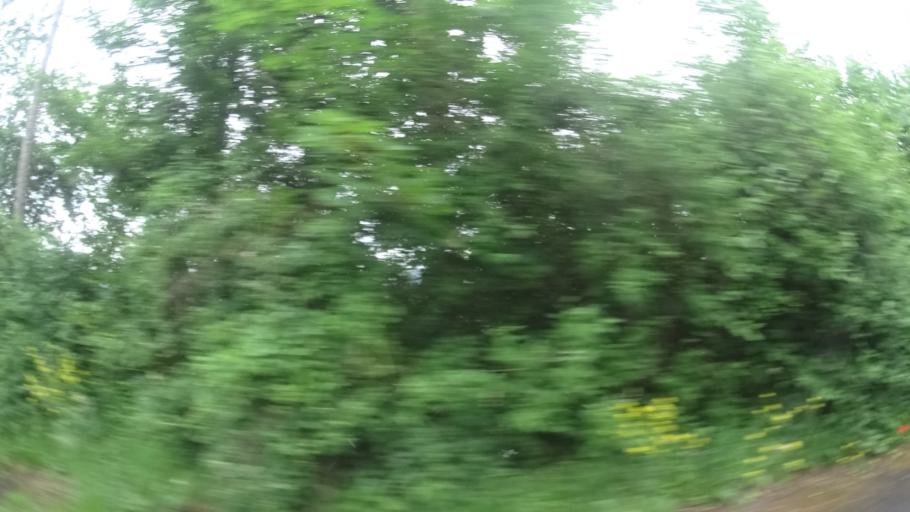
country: DE
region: Thuringia
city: Meiningen
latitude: 50.5852
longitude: 10.4045
